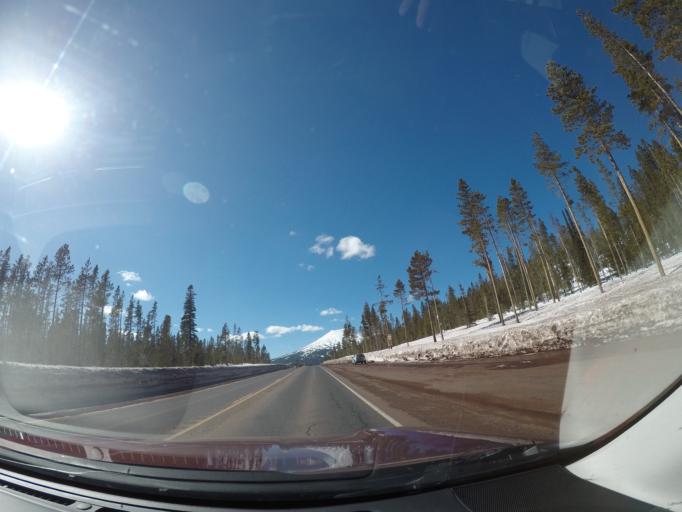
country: US
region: Oregon
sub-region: Deschutes County
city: Sunriver
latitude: 43.9837
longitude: -121.6058
